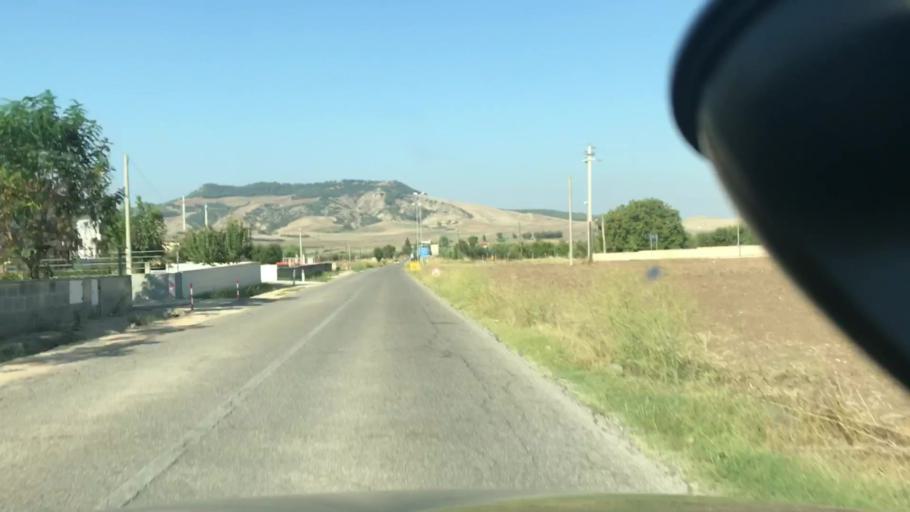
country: IT
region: Basilicate
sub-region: Provincia di Matera
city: La Martella
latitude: 40.6584
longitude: 16.5324
